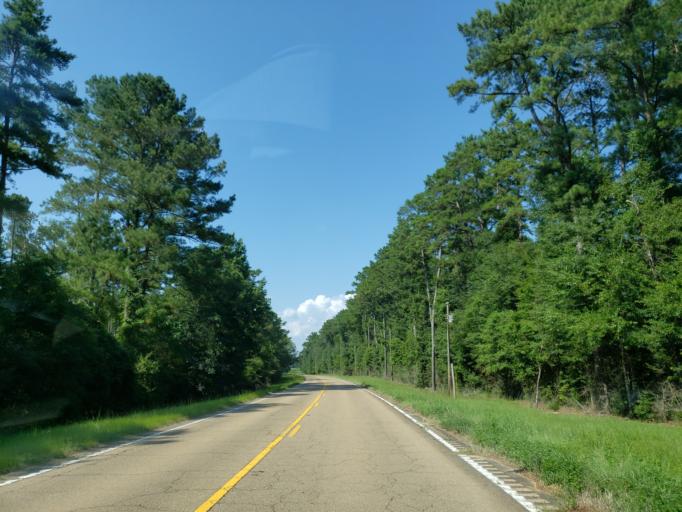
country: US
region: Mississippi
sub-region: Lamar County
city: Sumrall
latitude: 31.4445
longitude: -89.5295
